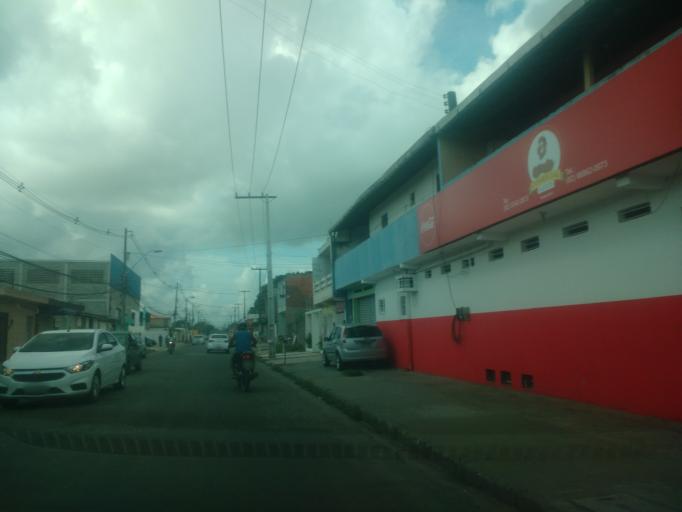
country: BR
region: Alagoas
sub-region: Satuba
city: Satuba
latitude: -9.5613
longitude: -35.7822
